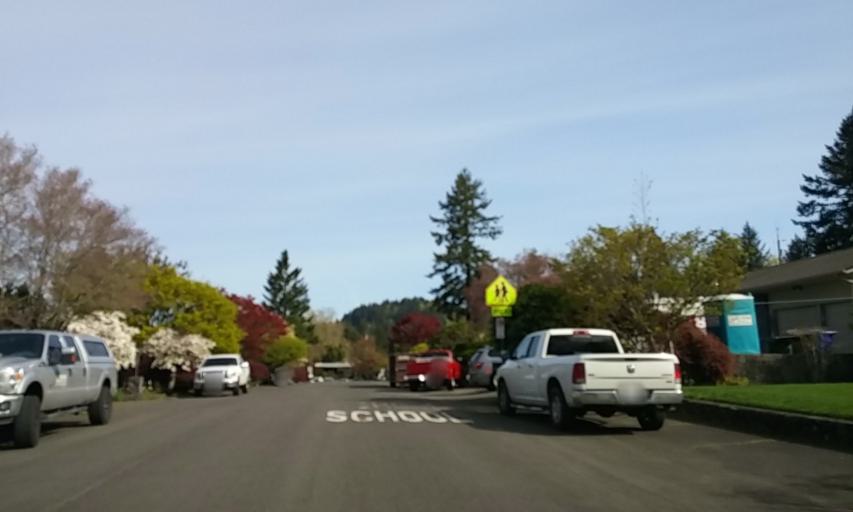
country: US
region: Oregon
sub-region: Washington County
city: West Slope
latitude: 45.5026
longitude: -122.7602
